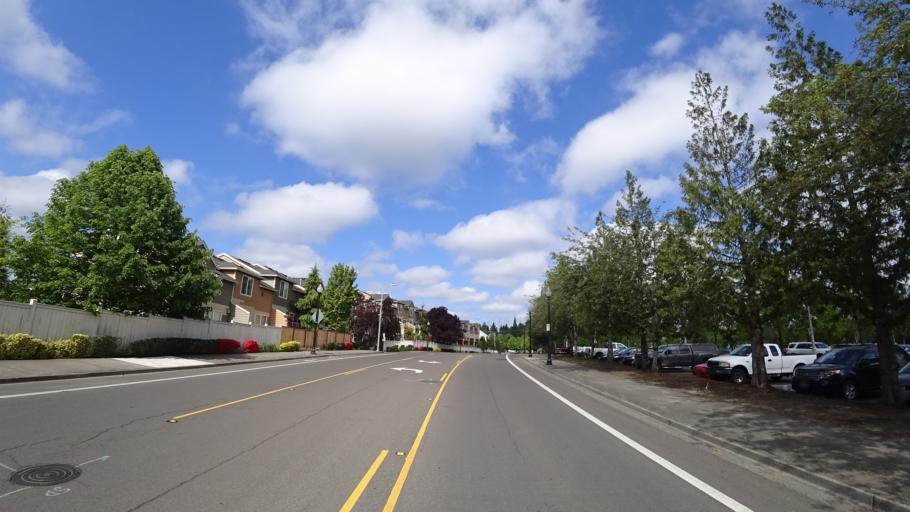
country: US
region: Oregon
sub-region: Washington County
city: Rockcreek
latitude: 45.5222
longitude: -122.8888
